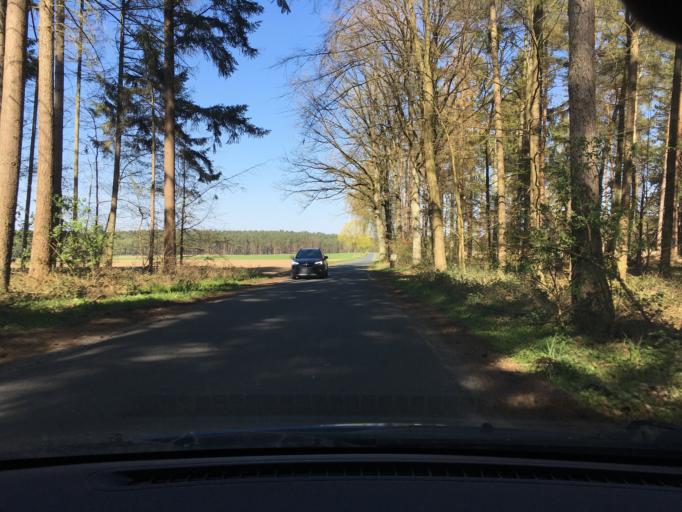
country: DE
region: Lower Saxony
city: Karwitz
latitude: 53.1181
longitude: 11.0047
